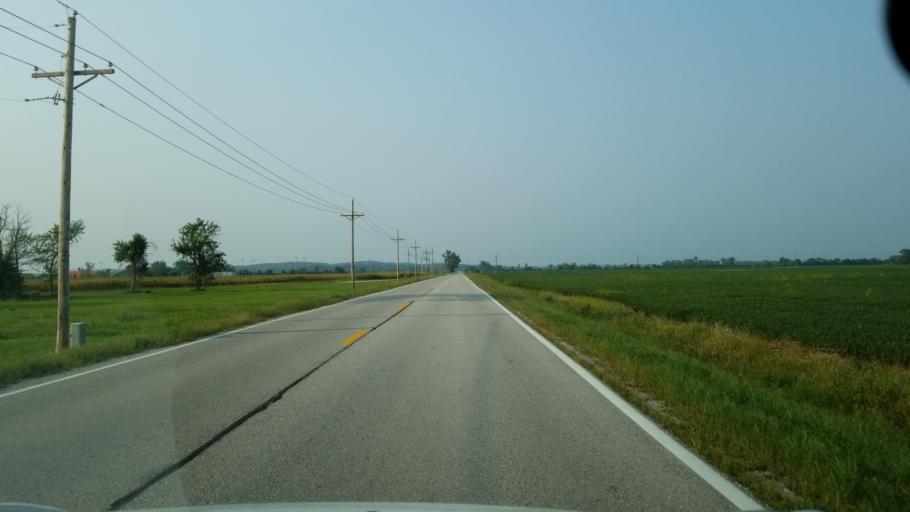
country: US
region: Nebraska
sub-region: Sarpy County
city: Offutt Air Force Base
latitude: 41.0970
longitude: -95.8898
